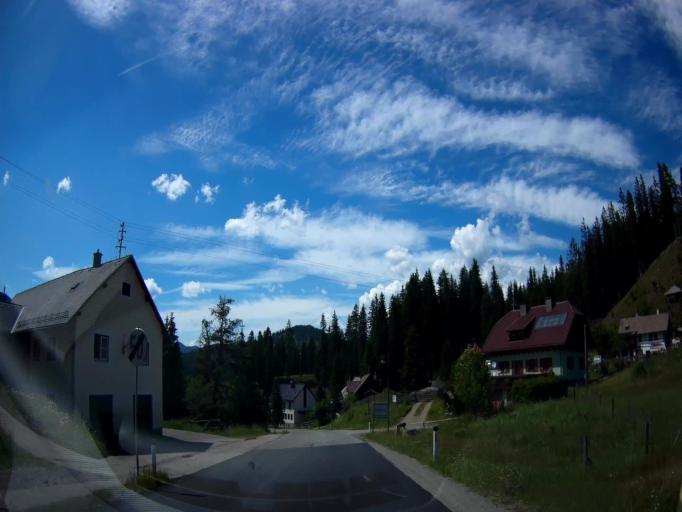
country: AT
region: Carinthia
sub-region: Politischer Bezirk Sankt Veit an der Glan
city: Glodnitz
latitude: 46.9419
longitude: 14.0354
